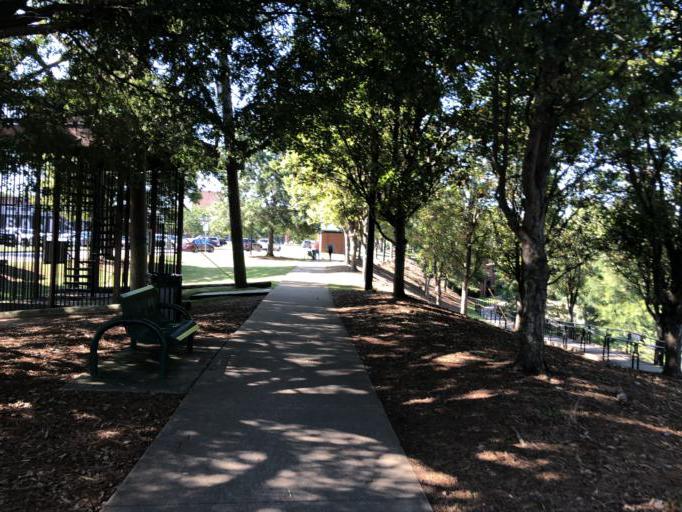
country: US
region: Alabama
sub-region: Russell County
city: Phenix City
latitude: 32.4666
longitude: -84.9959
